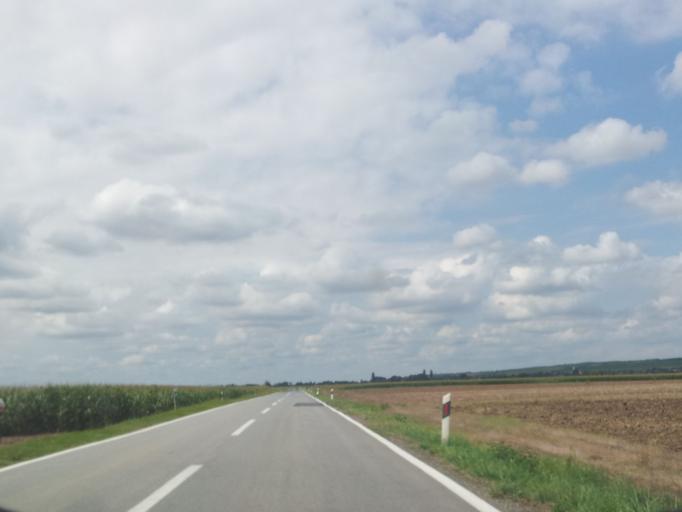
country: HR
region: Osjecko-Baranjska
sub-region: Grad Osijek
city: Karanac
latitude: 45.7473
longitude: 18.7123
